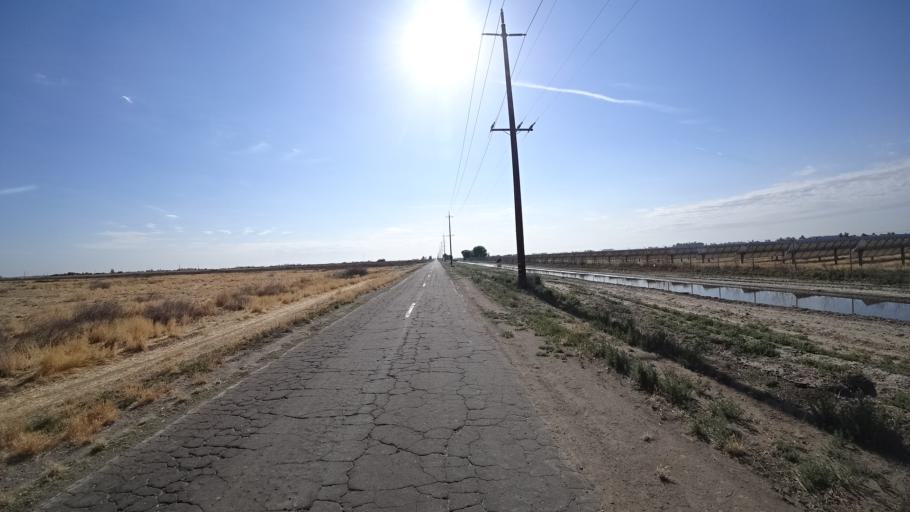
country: US
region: California
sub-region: Kings County
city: Stratford
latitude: 36.2261
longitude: -119.8286
